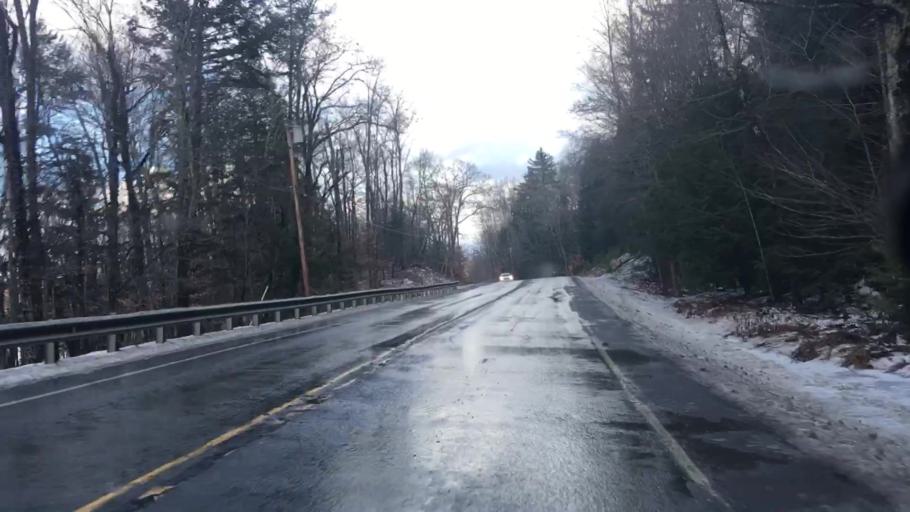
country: US
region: Maine
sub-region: Hancock County
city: Dedham
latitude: 44.6521
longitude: -68.6843
